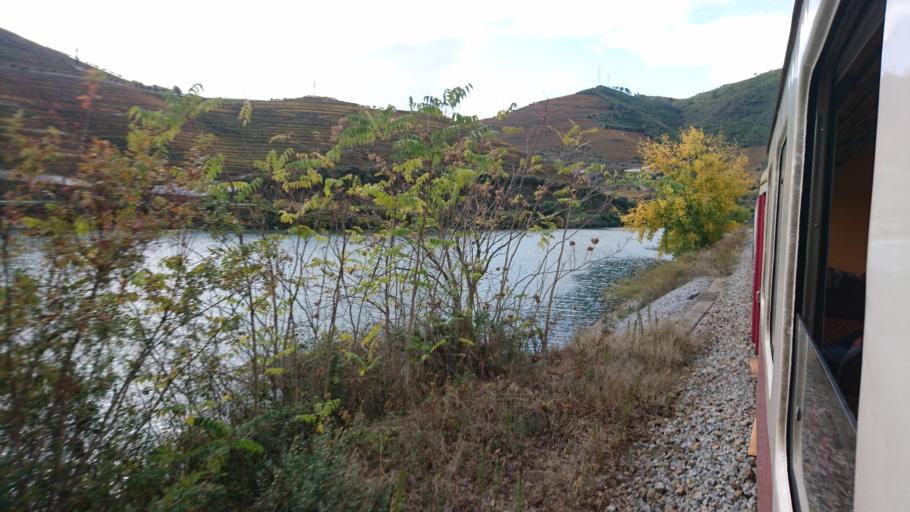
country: PT
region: Viseu
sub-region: Armamar
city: Armamar
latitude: 41.1444
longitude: -7.6936
